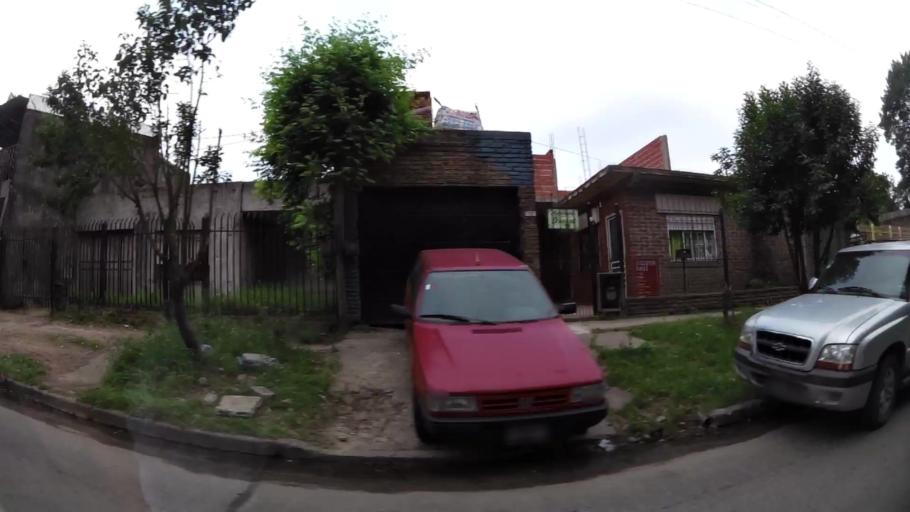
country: AR
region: Buenos Aires
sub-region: Partido de Moron
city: Moron
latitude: -34.6821
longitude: -58.5972
